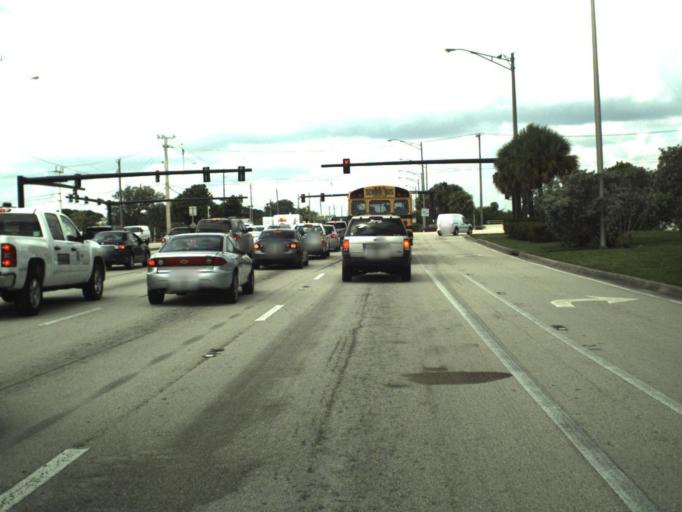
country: US
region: Florida
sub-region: Broward County
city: Davie
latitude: 26.0647
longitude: -80.2510
